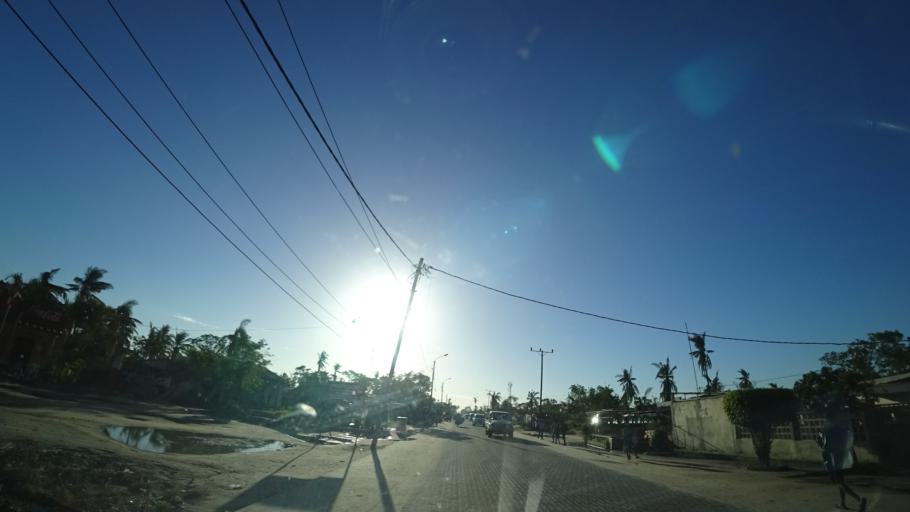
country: MZ
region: Sofala
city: Beira
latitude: -19.7497
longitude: 34.8534
